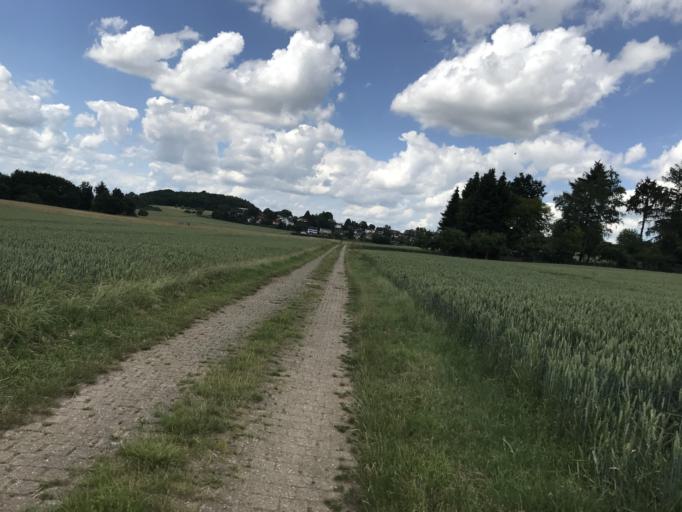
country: DE
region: Hesse
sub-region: Regierungsbezirk Giessen
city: Reiskirchen
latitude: 50.5840
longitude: 8.8345
